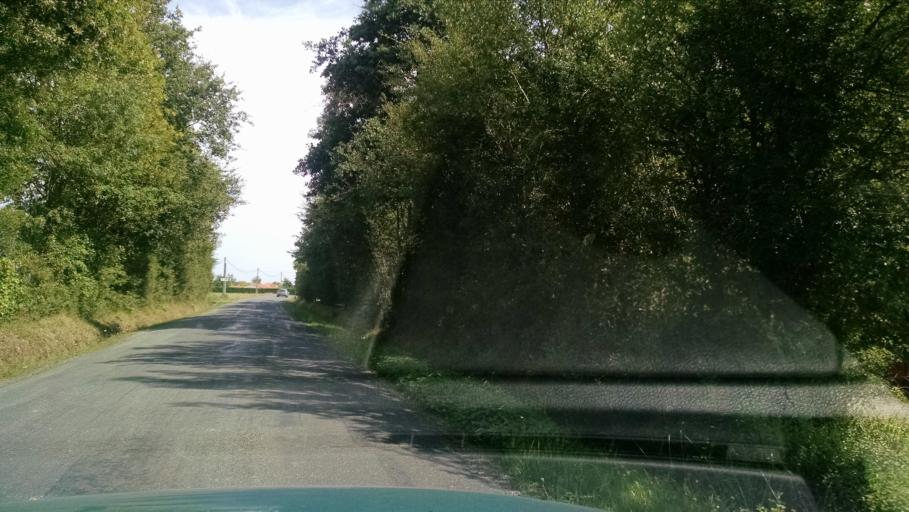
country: FR
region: Pays de la Loire
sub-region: Departement de la Loire-Atlantique
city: Clisson
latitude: 47.1014
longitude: -1.2757
